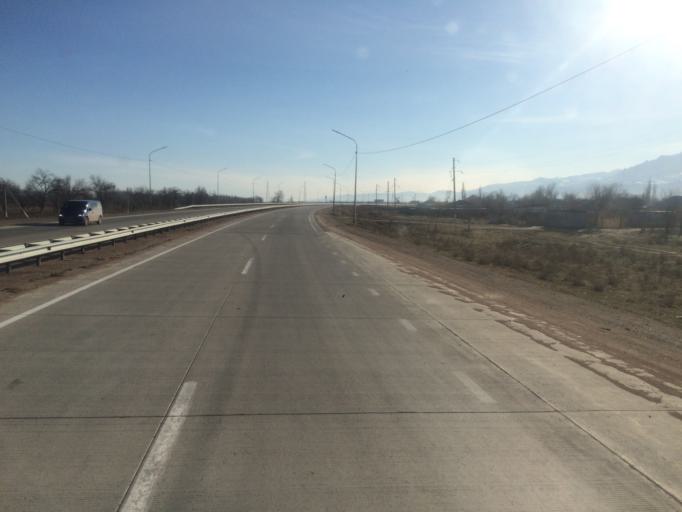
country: KG
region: Talas
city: Ivanovo-Alekseyevka
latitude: 42.9961
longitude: 72.1031
